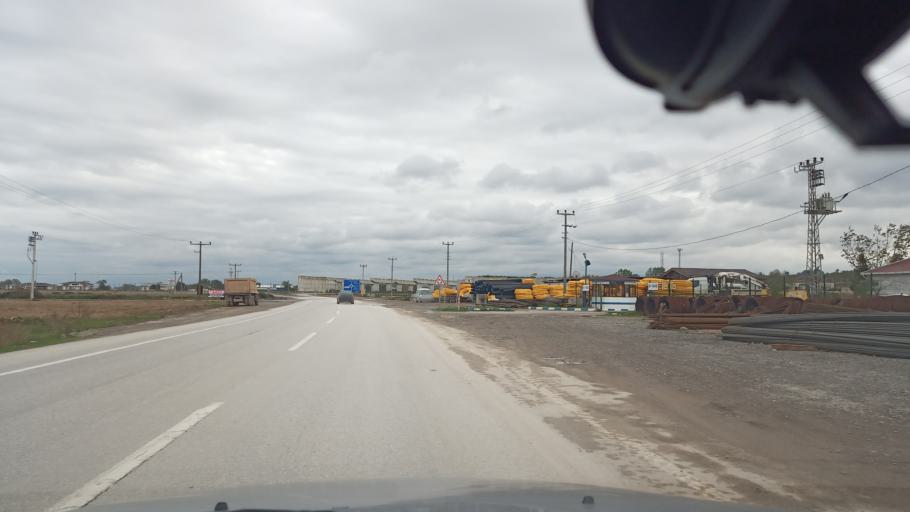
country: TR
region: Sakarya
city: Karasu
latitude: 41.1135
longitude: 30.6569
